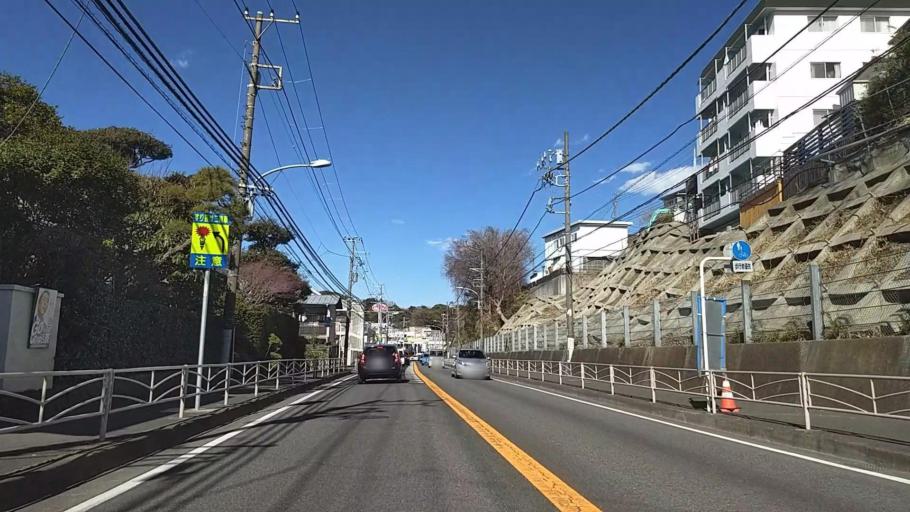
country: JP
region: Kanagawa
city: Yokohama
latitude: 35.3652
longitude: 139.6311
